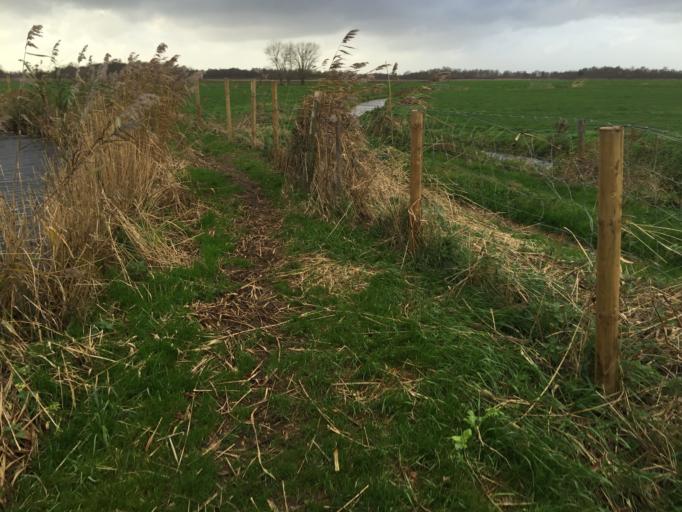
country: NL
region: North Holland
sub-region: Gemeente Ouder-Amstel
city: Ouderkerk aan de Amstel
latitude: 52.2528
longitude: 4.9397
